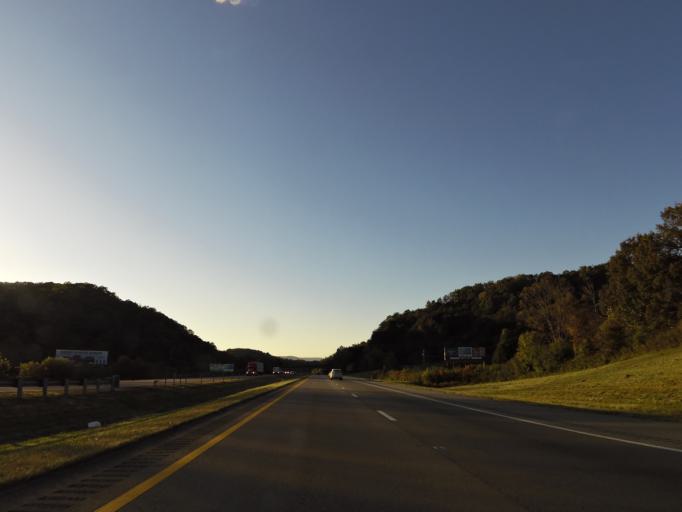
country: US
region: Tennessee
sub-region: Anderson County
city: Norris
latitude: 36.1427
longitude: -84.0497
